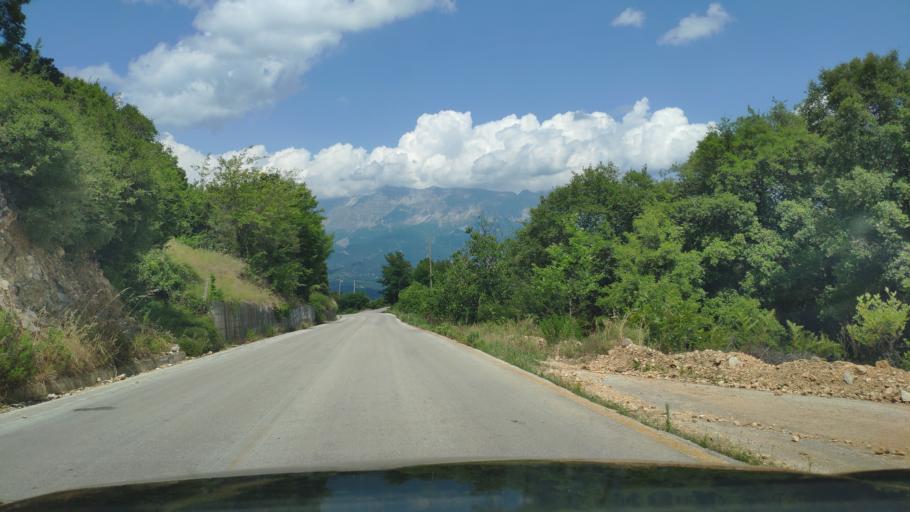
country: GR
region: Epirus
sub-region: Nomos Artas
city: Agios Dimitrios
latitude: 39.3505
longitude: 21.0141
